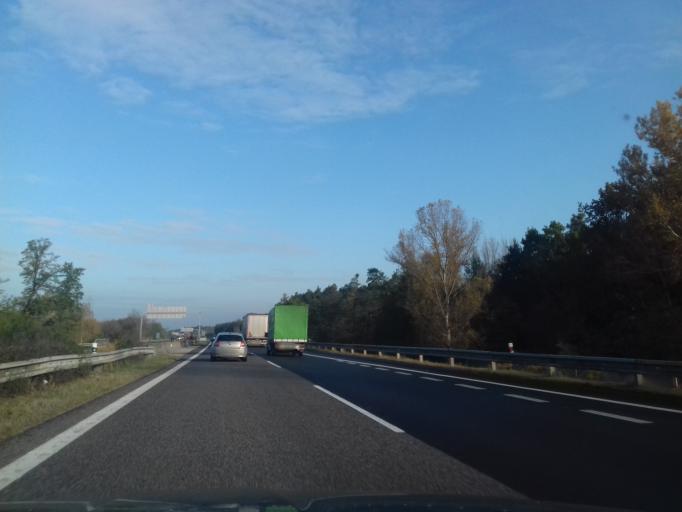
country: SK
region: Bratislavsky
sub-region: Okres Malacky
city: Malacky
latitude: 48.4319
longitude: 17.0429
